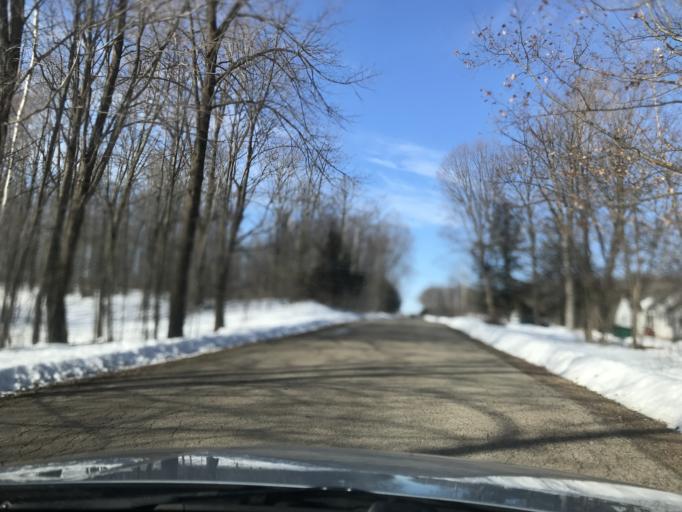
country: US
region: Wisconsin
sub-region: Oconto County
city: Gillett
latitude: 44.9391
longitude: -88.2227
